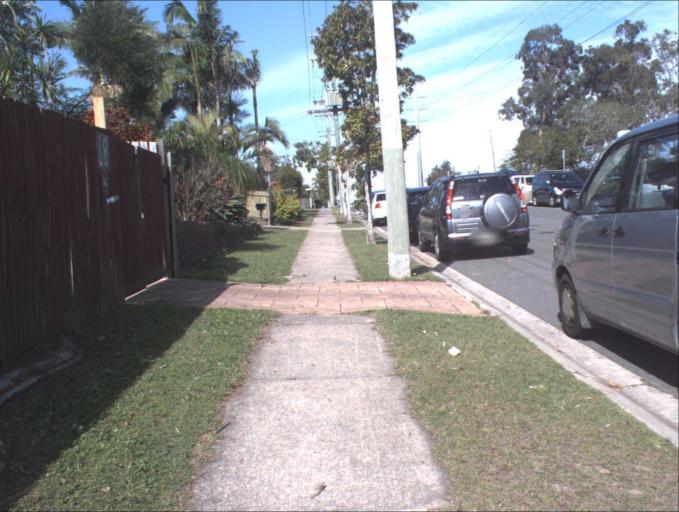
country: AU
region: Queensland
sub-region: Brisbane
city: Sunnybank Hills
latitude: -27.6674
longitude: 153.0540
